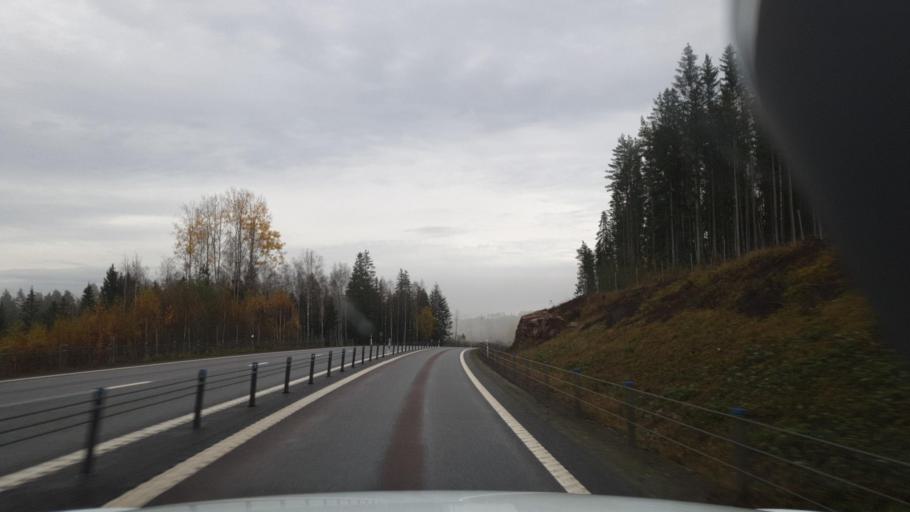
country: SE
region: Vaermland
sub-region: Arvika Kommun
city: Arvika
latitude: 59.6603
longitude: 12.7654
